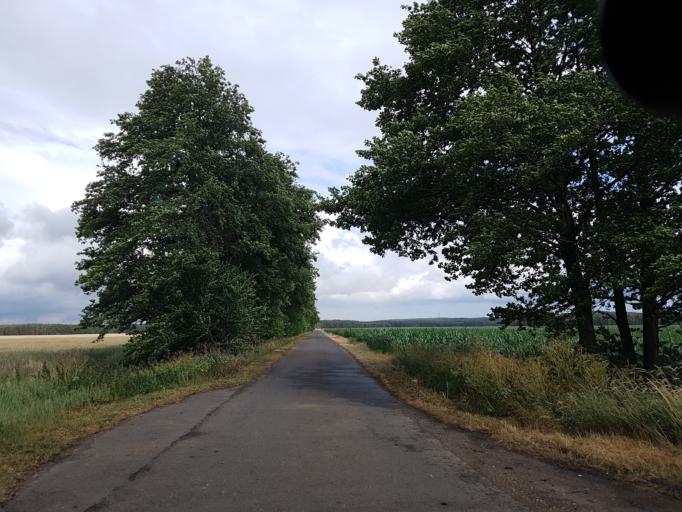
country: DE
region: Saxony-Anhalt
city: Jessen
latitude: 51.8344
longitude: 12.9507
